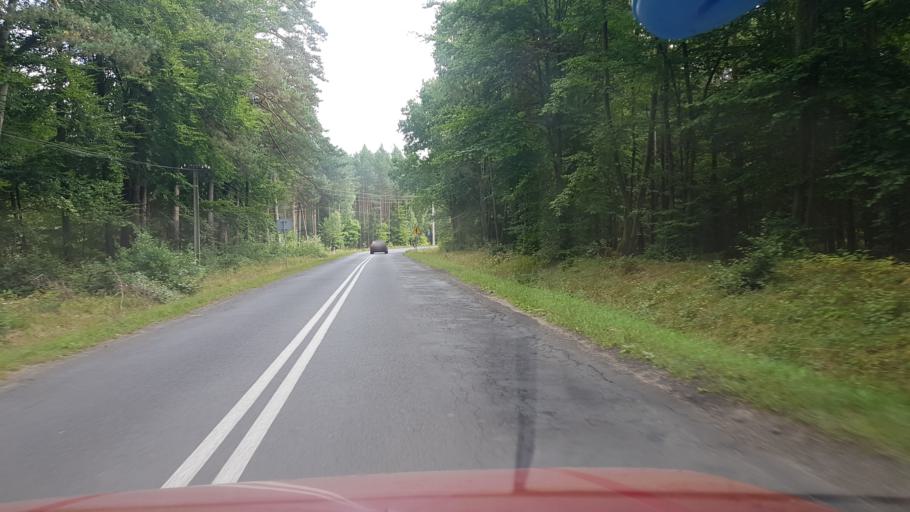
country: PL
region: West Pomeranian Voivodeship
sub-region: Powiat koszalinski
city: Polanow
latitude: 54.1163
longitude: 16.7122
